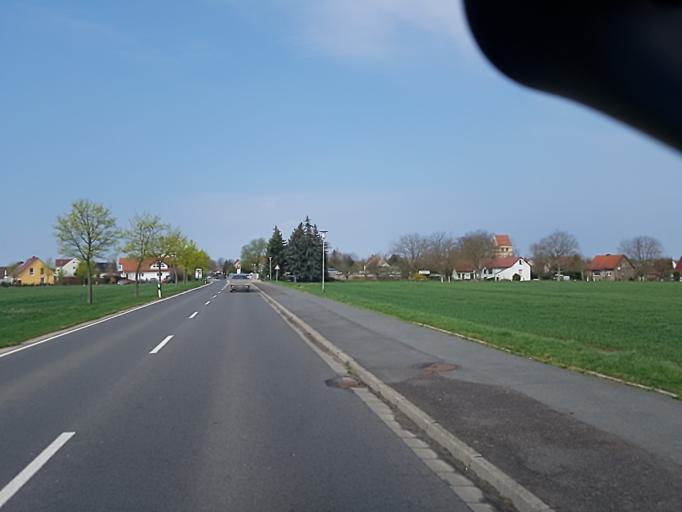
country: DE
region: Saxony
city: Zinna
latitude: 51.5660
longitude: 12.9619
